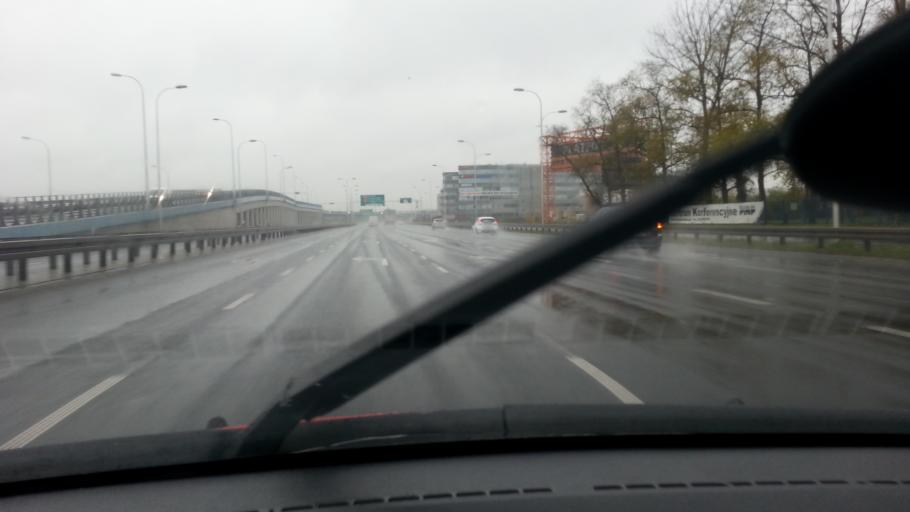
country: PL
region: Masovian Voivodeship
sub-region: Warszawa
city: Wlochy
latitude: 52.1927
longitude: 20.9234
